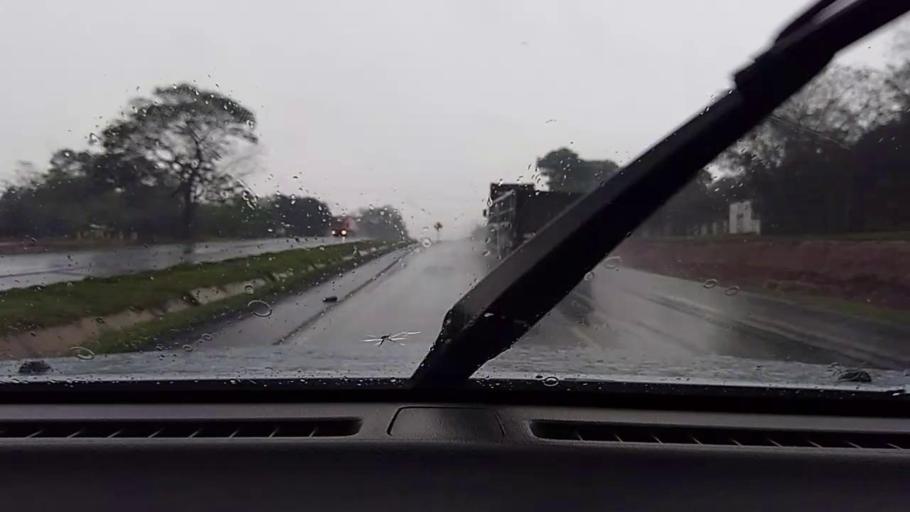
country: PY
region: Caaguazu
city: Repatriacion
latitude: -25.4457
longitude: -55.8850
